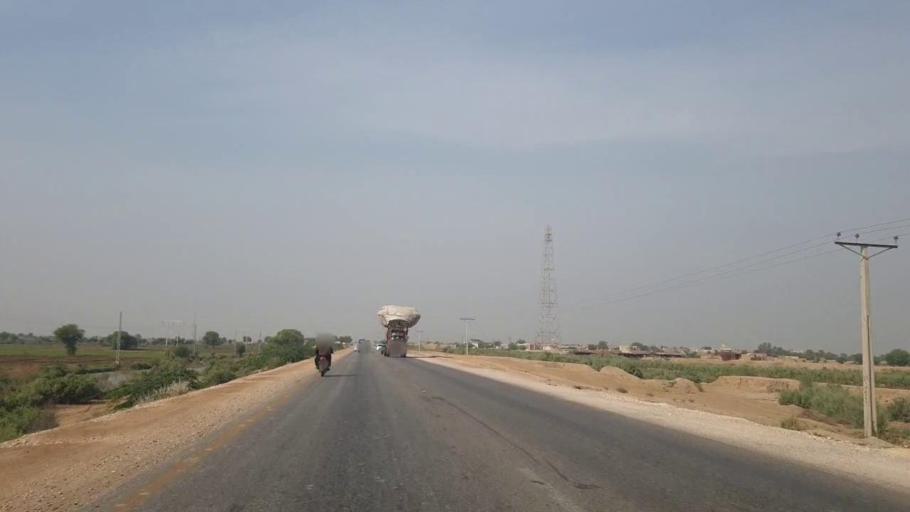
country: PK
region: Sindh
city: Sann
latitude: 26.0838
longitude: 68.0931
